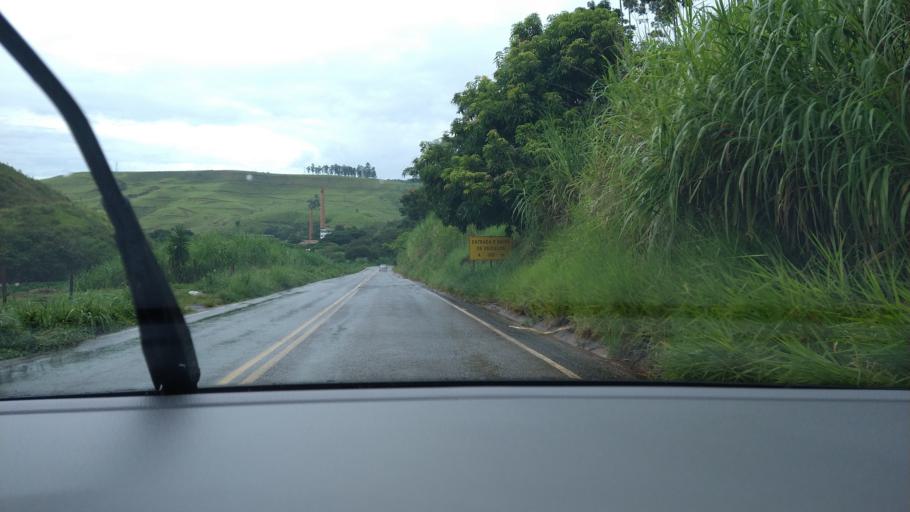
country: BR
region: Minas Gerais
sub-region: Ponte Nova
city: Ponte Nova
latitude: -20.3751
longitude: -42.8963
